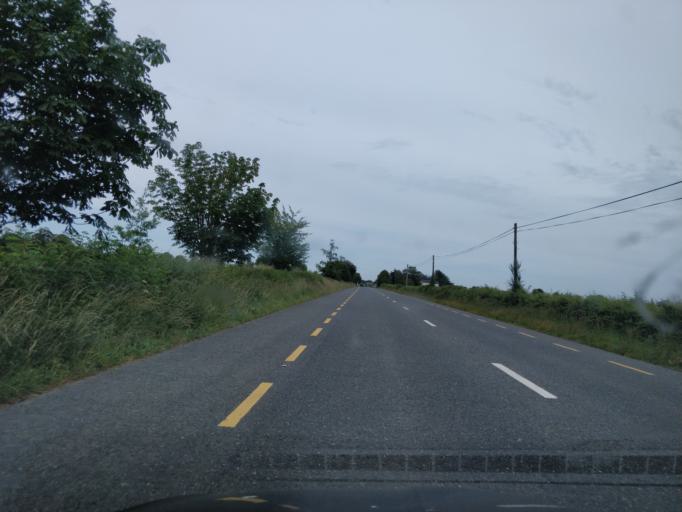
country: IE
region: Leinster
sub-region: Uibh Fhaili
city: Ferbane
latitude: 53.1710
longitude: -7.7451
